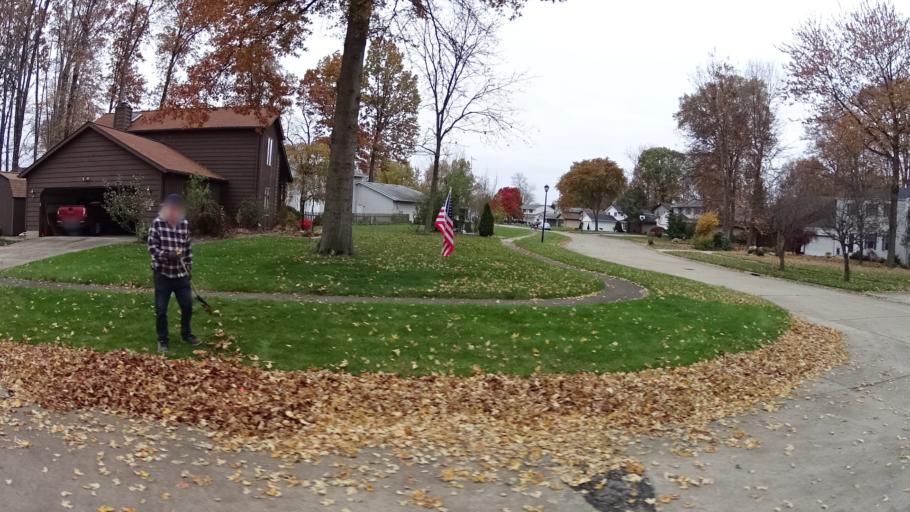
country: US
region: Ohio
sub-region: Lorain County
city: Sheffield
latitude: 41.4173
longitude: -82.0852
